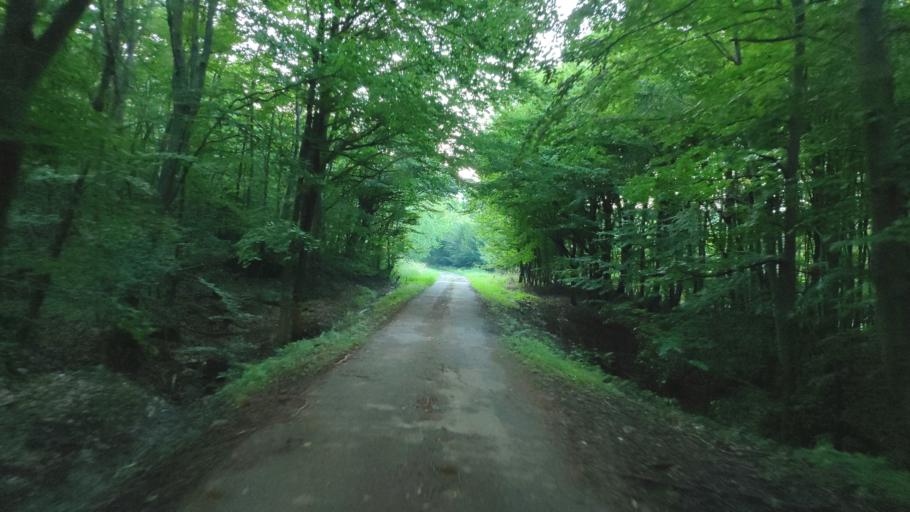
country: SK
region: Kosicky
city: Secovce
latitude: 48.5866
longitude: 21.5297
